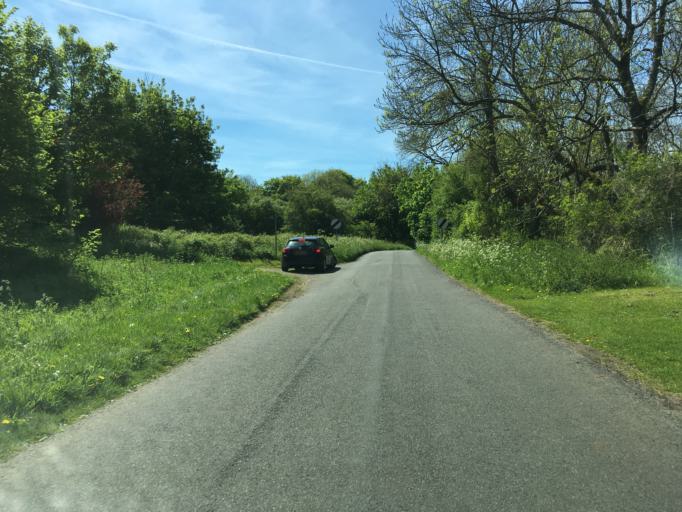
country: GB
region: England
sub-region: Gloucestershire
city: Coates
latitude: 51.7261
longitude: -2.0845
